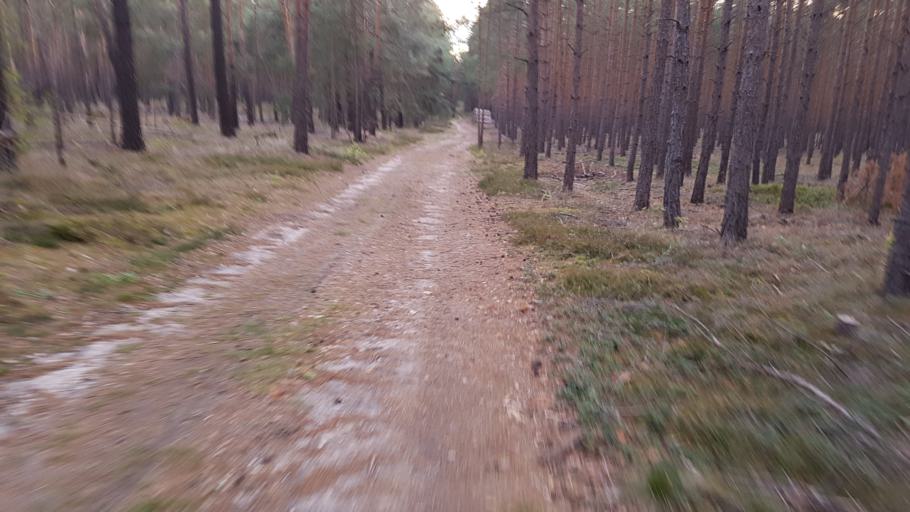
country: DE
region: Brandenburg
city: Trobitz
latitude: 51.5536
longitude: 13.4358
